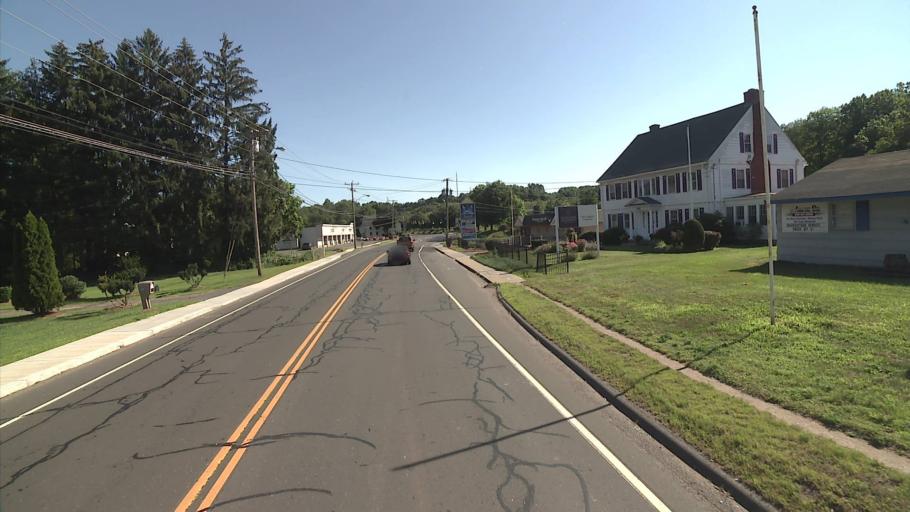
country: US
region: Connecticut
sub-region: Hartford County
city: Plainville
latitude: 41.6121
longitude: -72.8756
